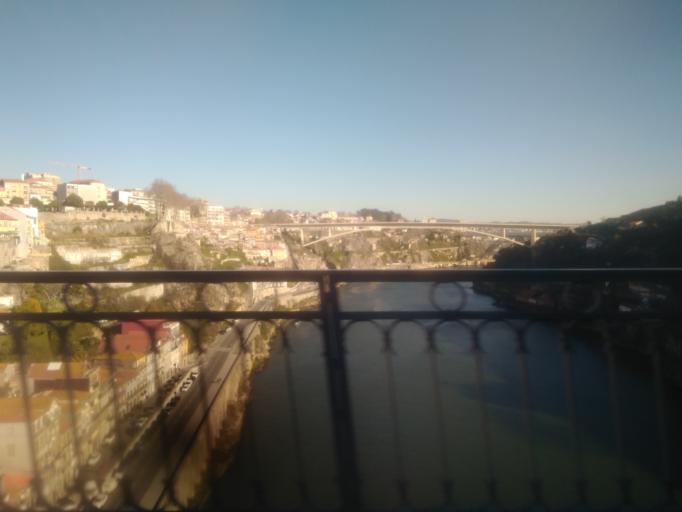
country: PT
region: Porto
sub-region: Porto
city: Porto
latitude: 41.1405
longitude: -8.6095
